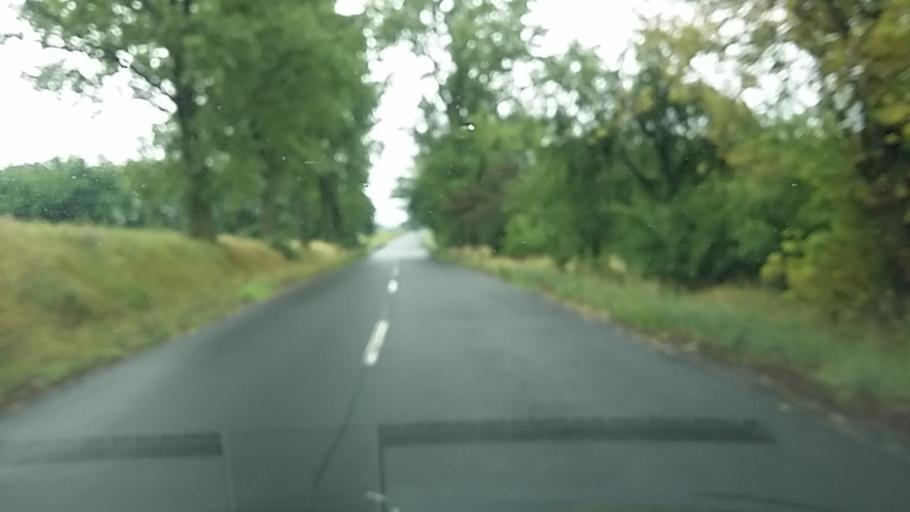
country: HU
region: Komarom-Esztergom
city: Esztergom
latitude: 47.9387
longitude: 18.7766
